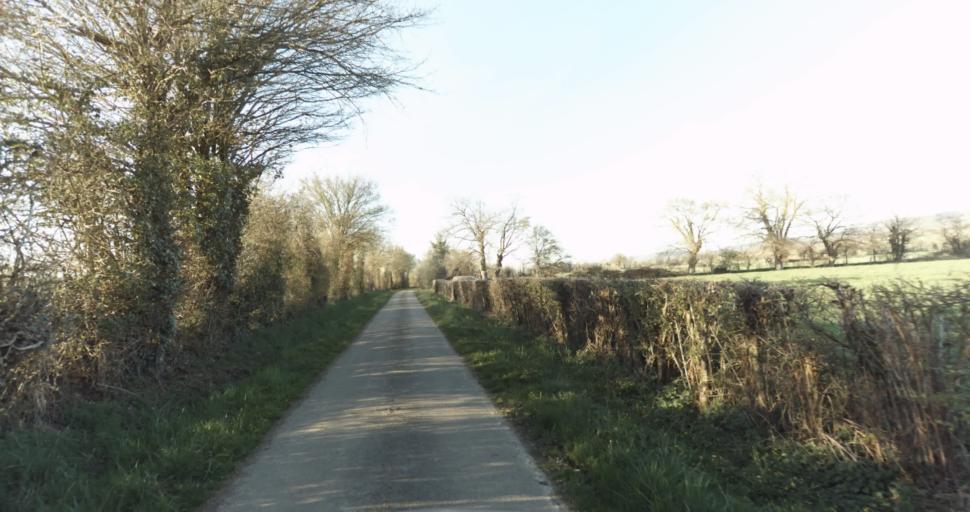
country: FR
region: Lower Normandy
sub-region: Departement de l'Orne
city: Trun
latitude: 48.9057
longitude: 0.0179
